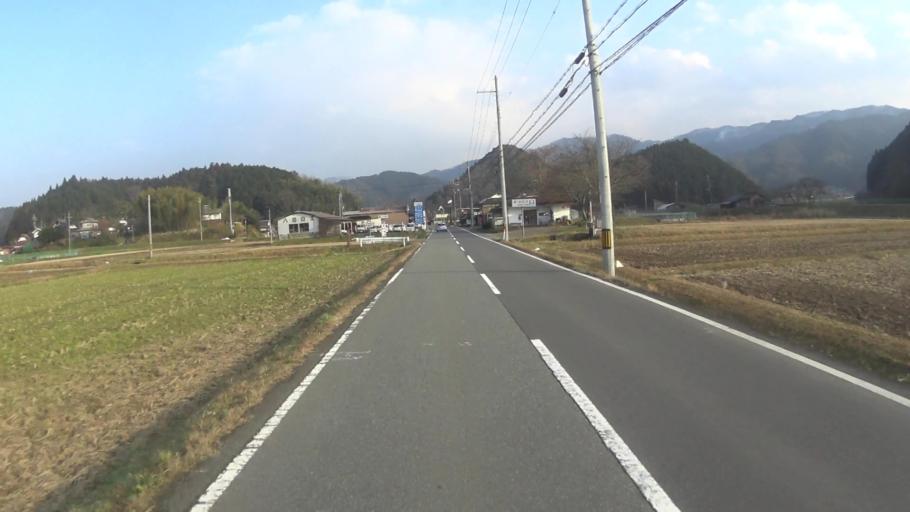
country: JP
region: Kyoto
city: Maizuru
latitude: 35.3688
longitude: 135.4206
